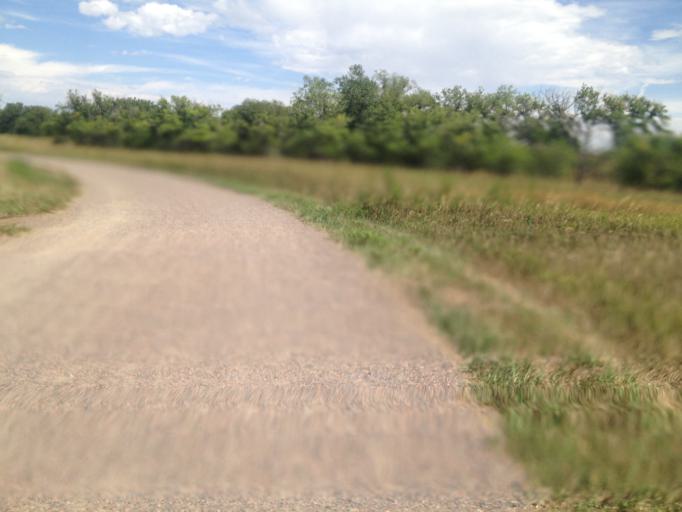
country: US
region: Colorado
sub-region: Boulder County
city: Louisville
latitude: 39.9662
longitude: -105.1348
